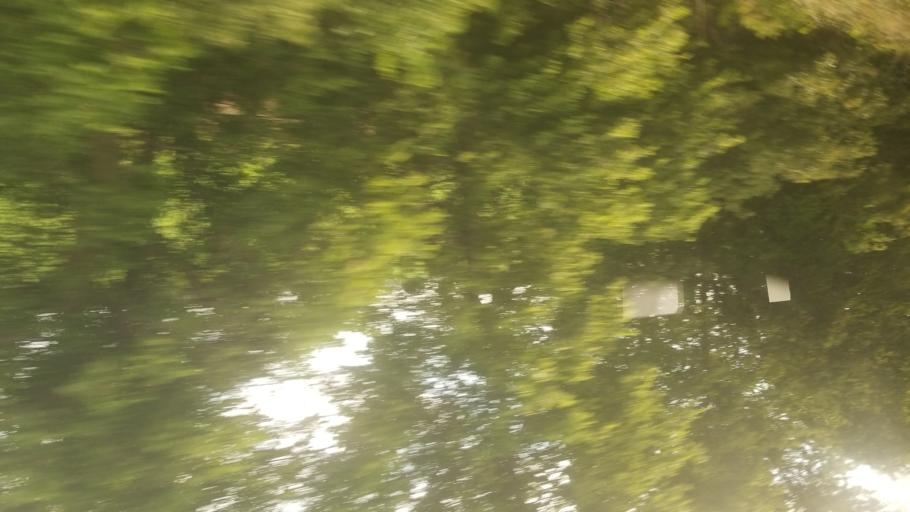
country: US
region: Kansas
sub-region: Douglas County
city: Eudora
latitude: 38.9499
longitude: -95.1647
